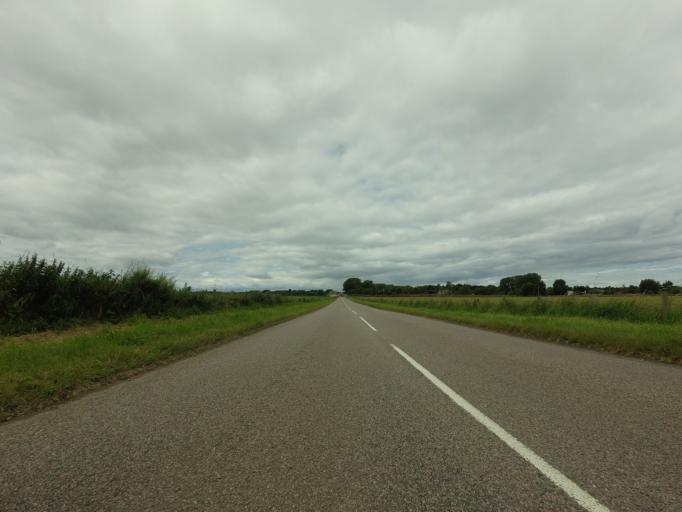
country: GB
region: Scotland
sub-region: Moray
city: Kinloss
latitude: 57.6303
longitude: -3.5539
